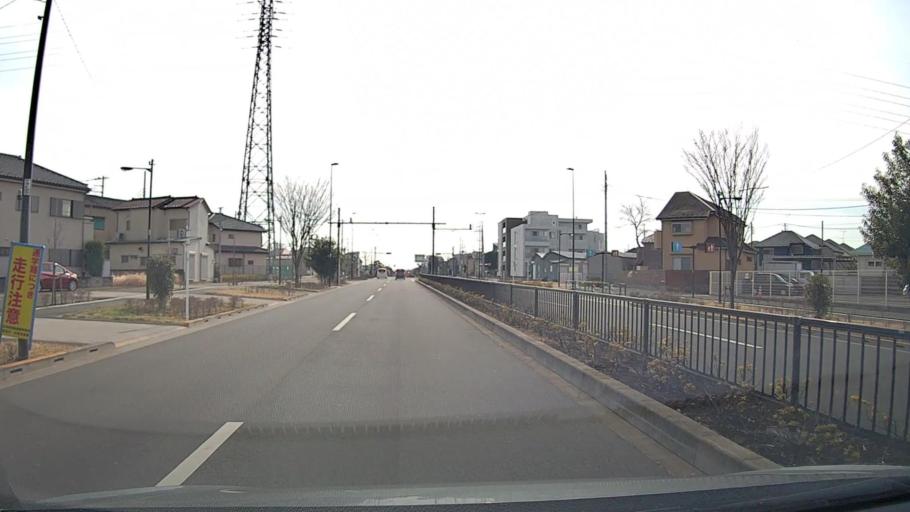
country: JP
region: Tokyo
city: Tanashicho
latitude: 35.7592
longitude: 139.5611
